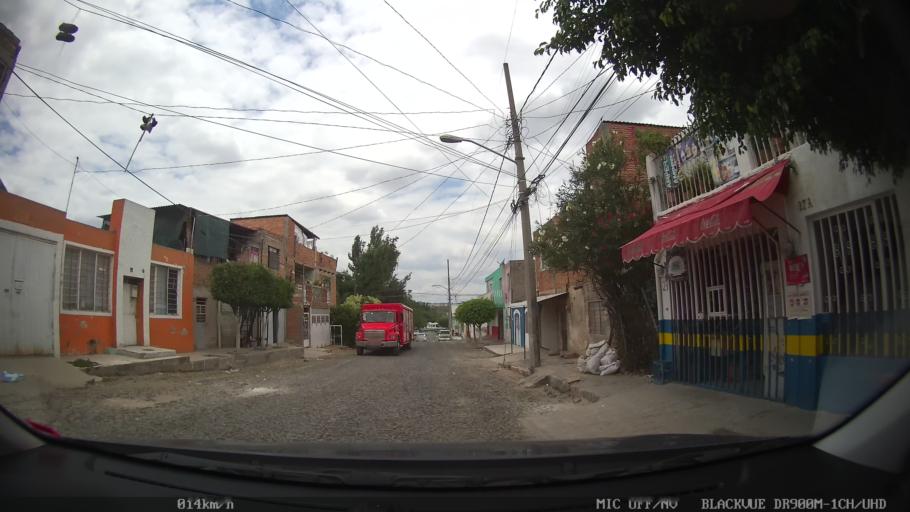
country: MX
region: Jalisco
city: Tlaquepaque
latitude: 20.6538
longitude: -103.2621
